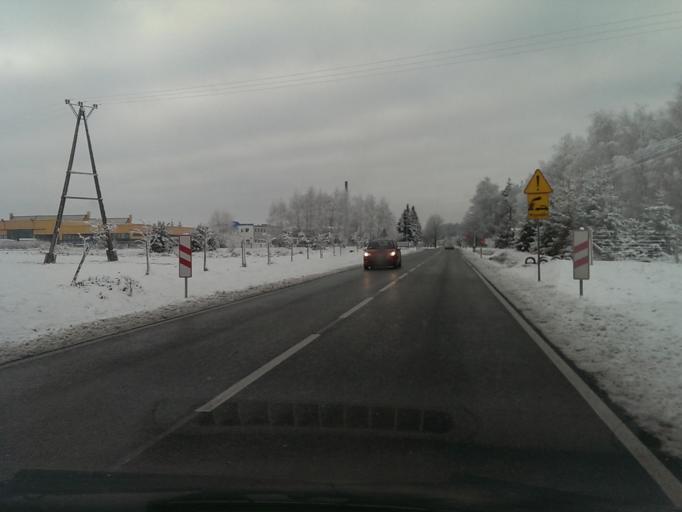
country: PL
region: Kujawsko-Pomorskie
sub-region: Powiat sepolenski
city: Sepolno Krajenskie
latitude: 53.4365
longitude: 17.5494
